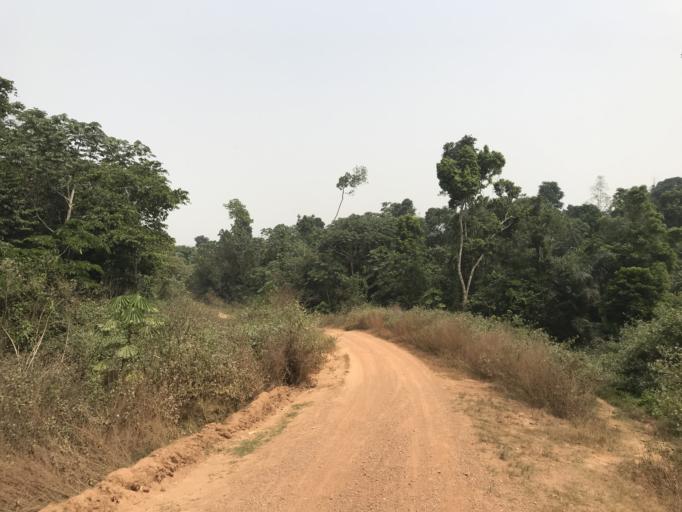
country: NG
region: Osun
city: Ifetedo
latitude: 7.0448
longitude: 4.4639
